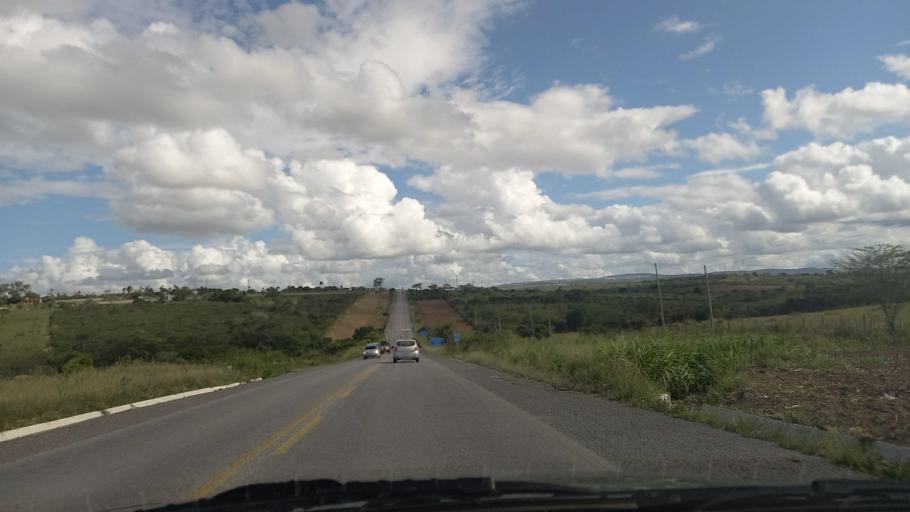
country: BR
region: Pernambuco
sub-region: Sao Joao
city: Sao Joao
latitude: -8.7955
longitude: -36.4369
